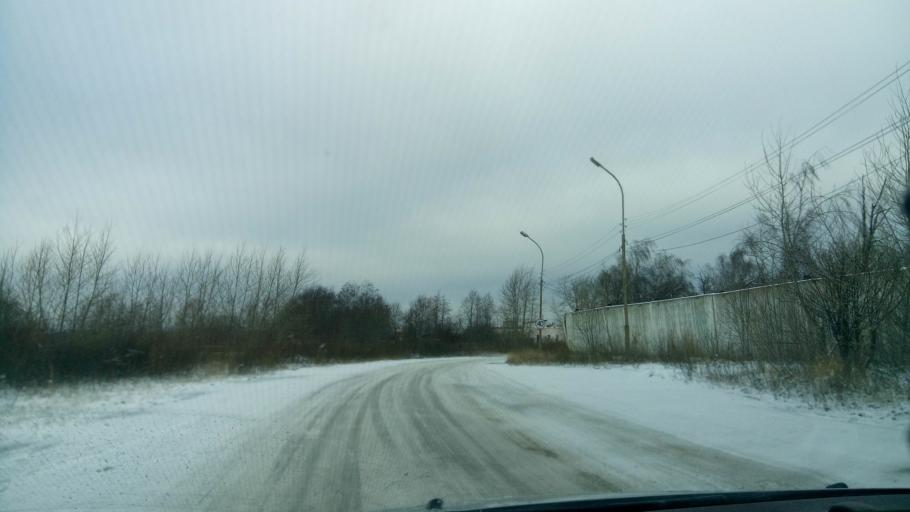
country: RU
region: Sverdlovsk
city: Polevskoy
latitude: 56.4651
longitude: 60.1795
